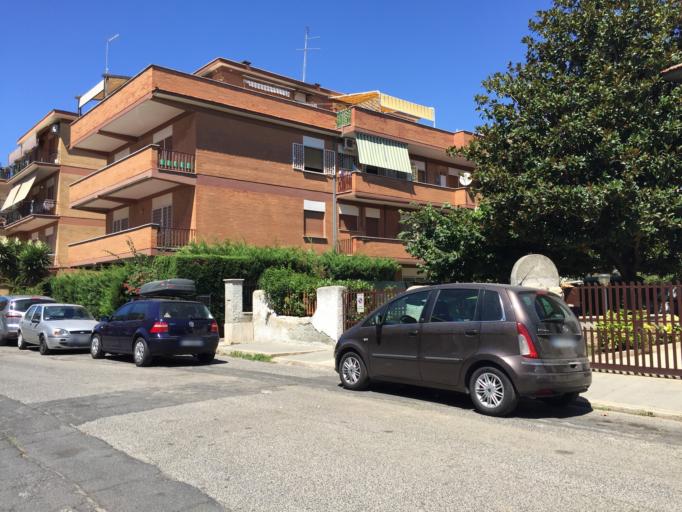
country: IT
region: Latium
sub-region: Citta metropolitana di Roma Capitale
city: Ladispoli
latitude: 41.9549
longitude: 12.0652
